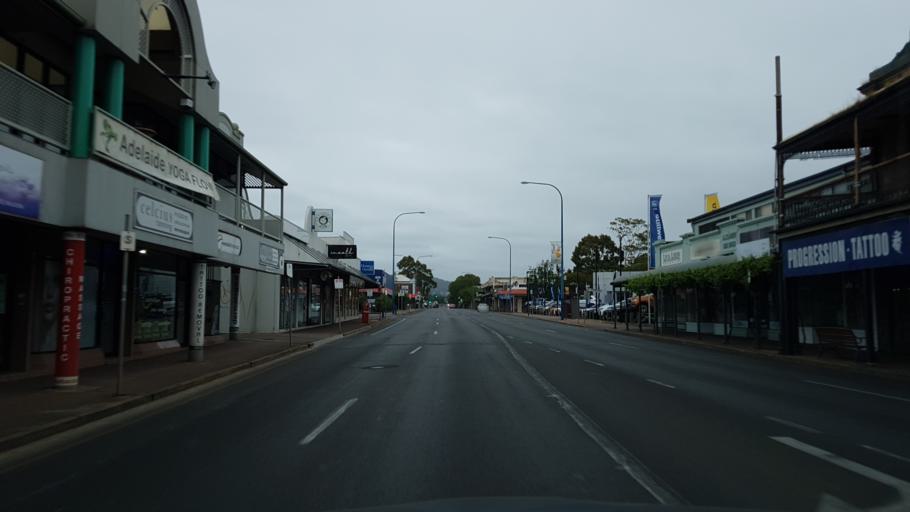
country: AU
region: South Australia
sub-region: Unley
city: Unley Park
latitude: -34.9550
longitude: 138.6079
